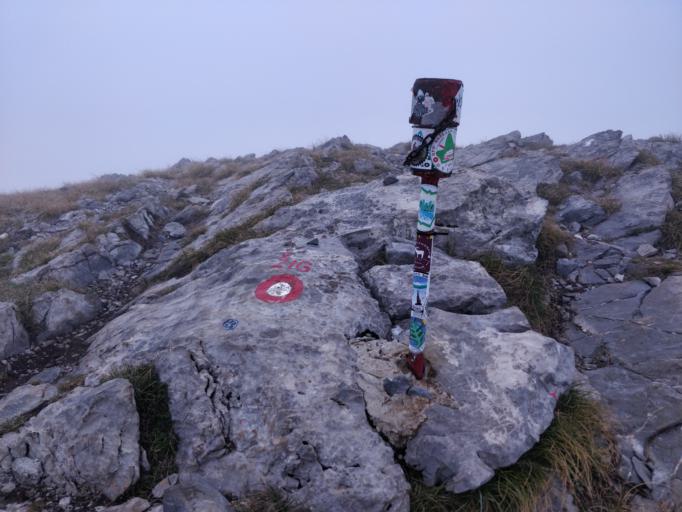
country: HR
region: Zadarska
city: Starigrad
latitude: 44.3677
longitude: 15.5046
